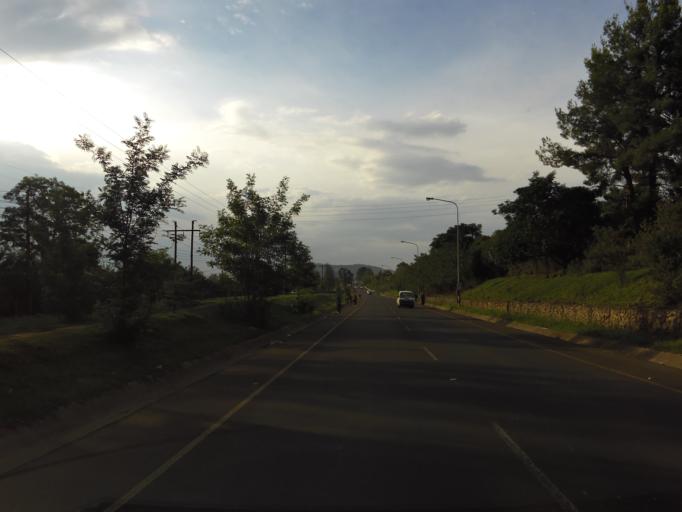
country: LS
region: Maseru
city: Maseru
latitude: -29.3147
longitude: 27.4703
